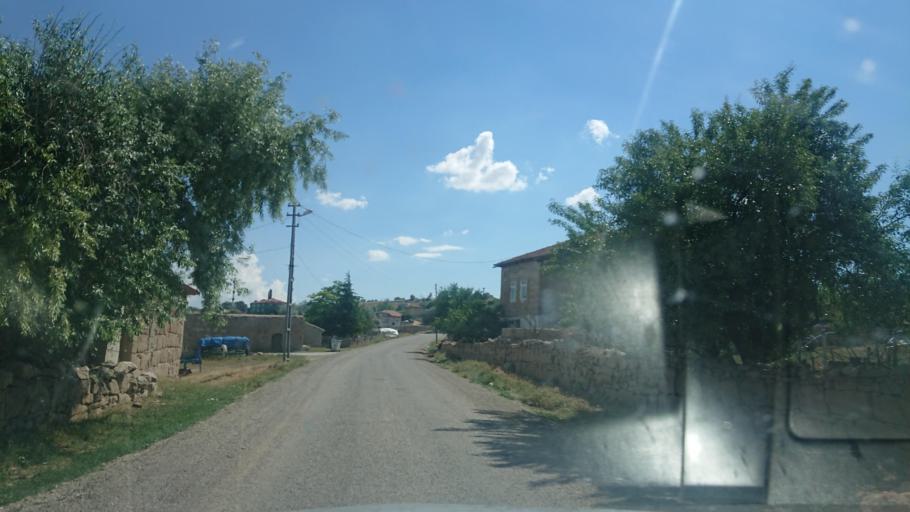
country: TR
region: Aksaray
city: Agacoren
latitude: 38.7740
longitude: 33.7868
